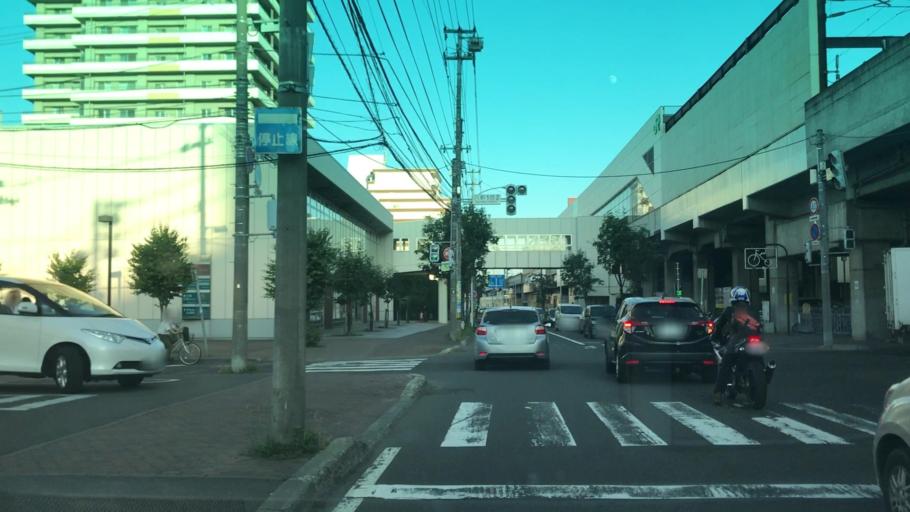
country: JP
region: Hokkaido
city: Sapporo
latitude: 43.0824
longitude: 141.3063
